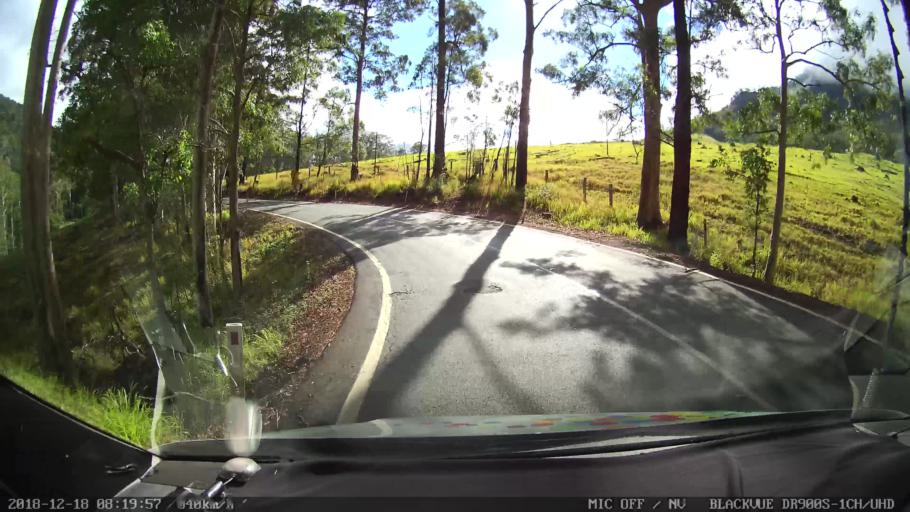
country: AU
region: New South Wales
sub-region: Kyogle
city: Kyogle
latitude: -28.3310
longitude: 152.7121
